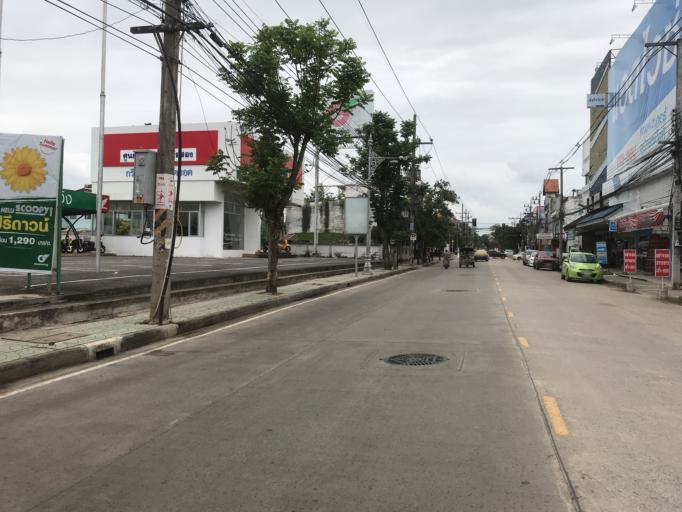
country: TH
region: Chiang Rai
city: Chiang Rai
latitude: 19.9020
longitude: 99.8327
